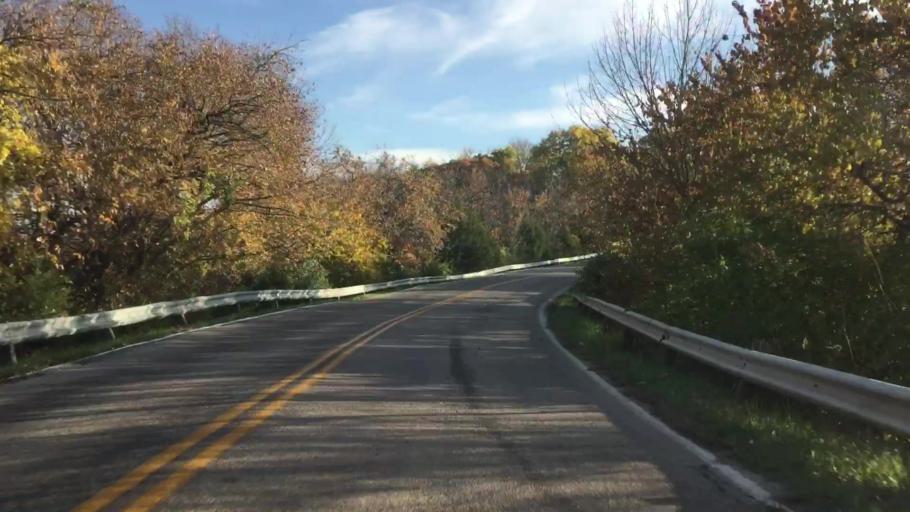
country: US
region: Kansas
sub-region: Wyandotte County
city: Edwardsville
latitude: 39.0186
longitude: -94.7798
